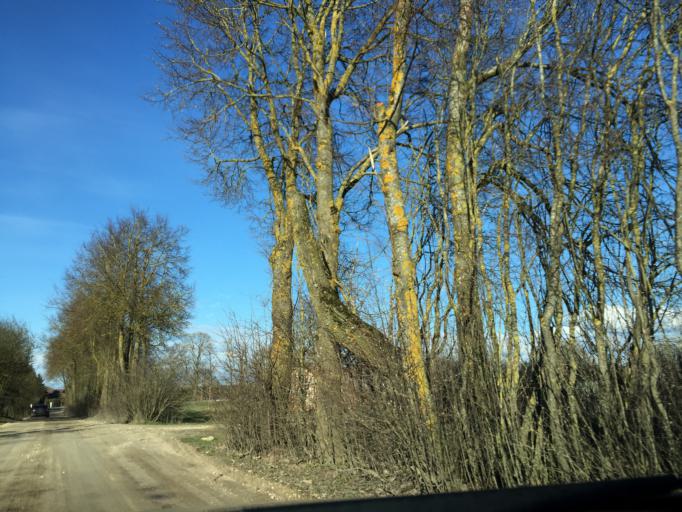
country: LV
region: Kekava
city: Kekava
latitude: 56.8449
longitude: 24.2040
